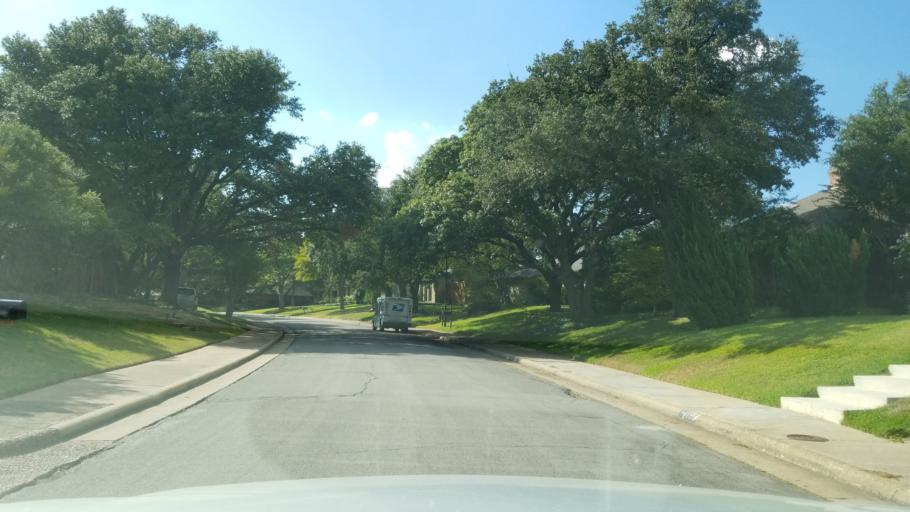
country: US
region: Texas
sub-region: Dallas County
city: Addison
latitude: 32.9646
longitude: -96.7980
